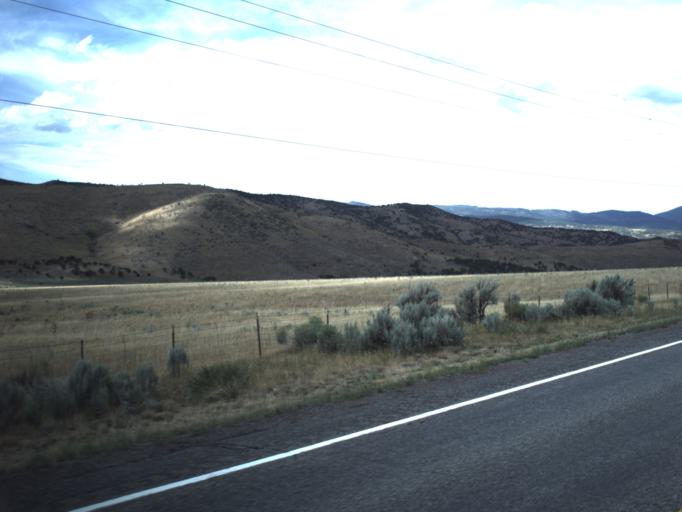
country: US
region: Utah
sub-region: Utah County
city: Woodland Hills
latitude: 39.8428
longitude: -111.5147
